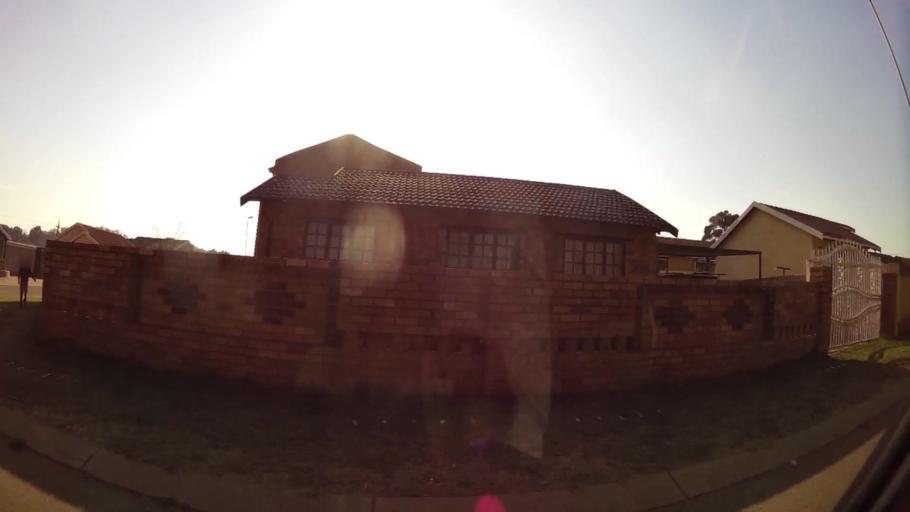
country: ZA
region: Gauteng
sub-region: City of Johannesburg Metropolitan Municipality
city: Soweto
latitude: -26.2884
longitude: 27.9491
